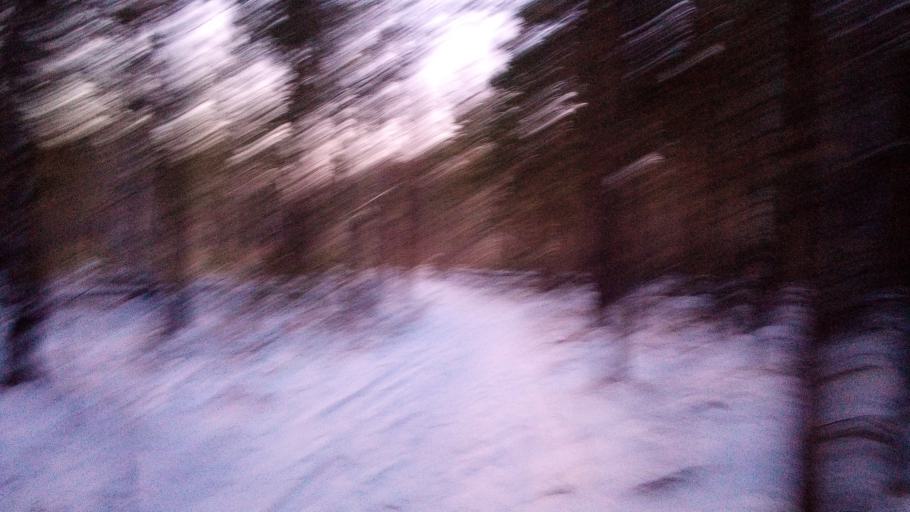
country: RU
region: Chelyabinsk
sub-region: Gorod Chelyabinsk
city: Chelyabinsk
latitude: 55.1645
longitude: 61.3316
